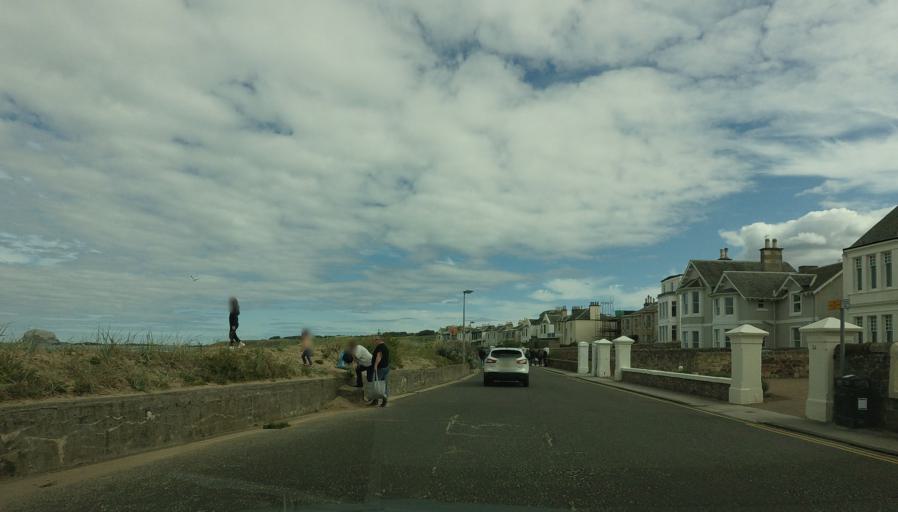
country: GB
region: Scotland
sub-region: East Lothian
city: North Berwick
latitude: 56.0583
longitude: -2.7122
